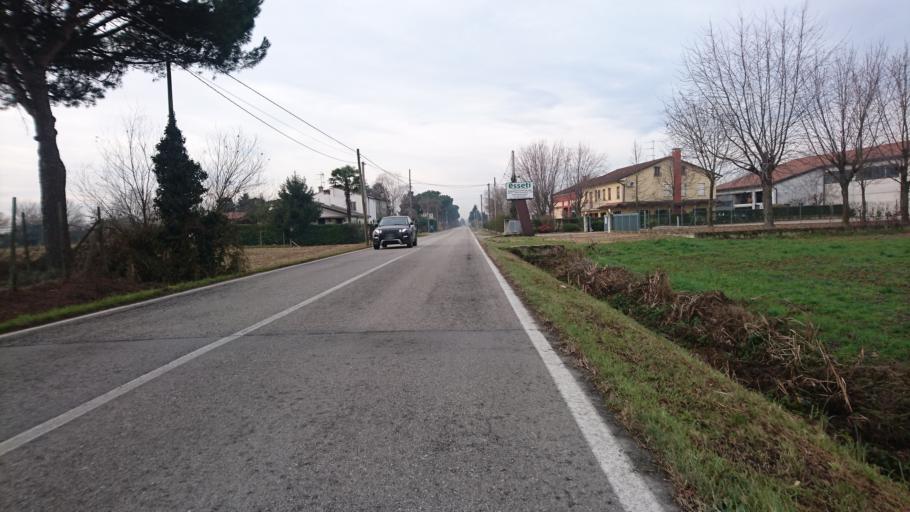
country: IT
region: Veneto
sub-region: Provincia di Padova
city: Campodoro
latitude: 45.4829
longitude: 11.7628
